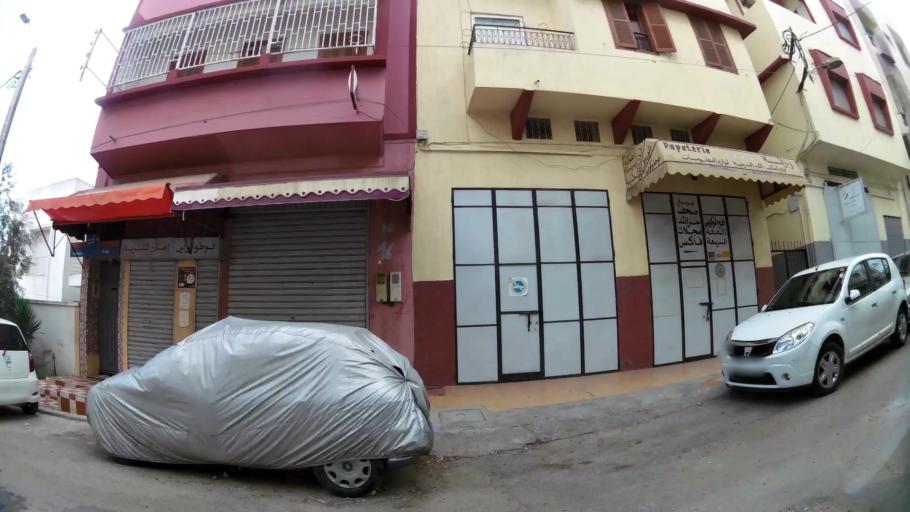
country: MA
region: Gharb-Chrarda-Beni Hssen
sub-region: Kenitra Province
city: Kenitra
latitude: 34.2652
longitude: -6.5664
